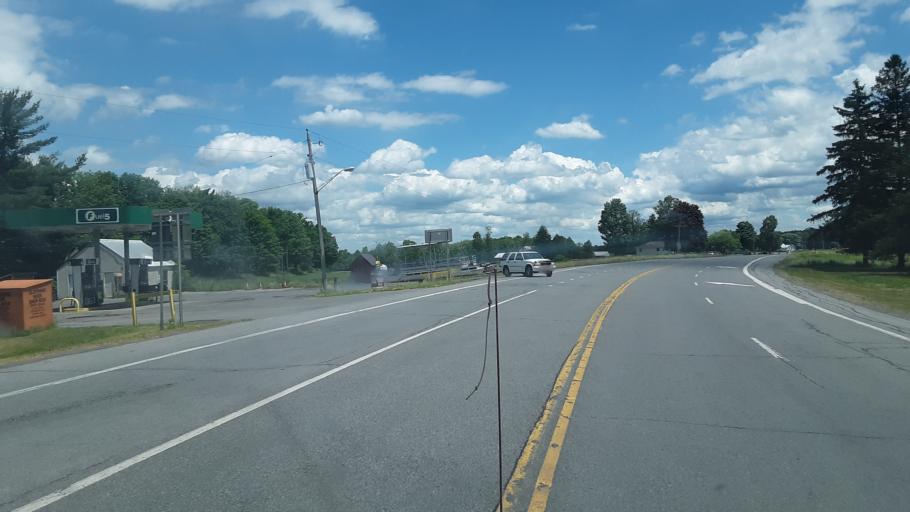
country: US
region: New York
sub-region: Oneida County
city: Rome
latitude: 43.2102
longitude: -75.5889
